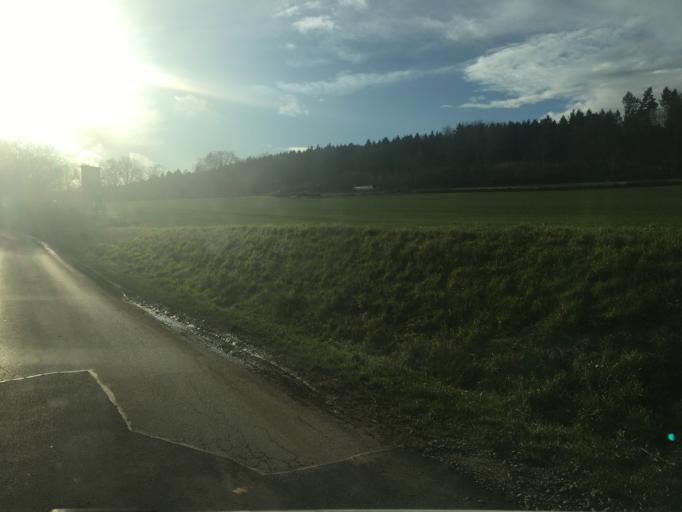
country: DE
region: North Rhine-Westphalia
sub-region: Regierungsbezirk Koln
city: Langerwehe
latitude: 50.8029
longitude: 6.3820
